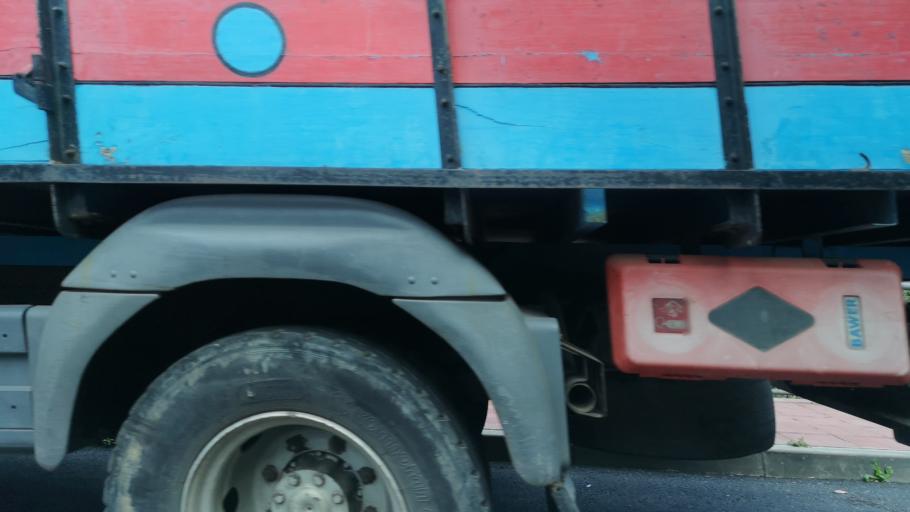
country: ES
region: Canary Islands
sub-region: Provincia de Santa Cruz de Tenerife
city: Hermigua
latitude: 28.1670
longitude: -17.1952
